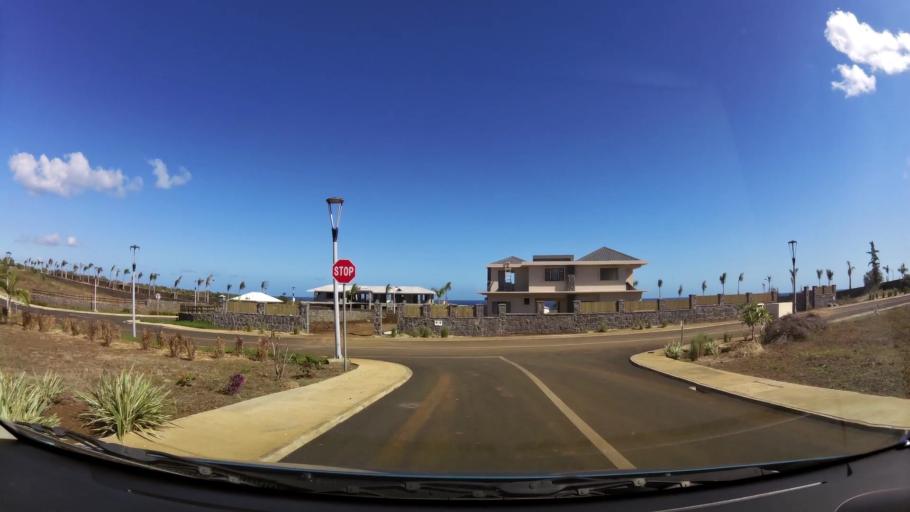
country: MU
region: Black River
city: Flic en Flac
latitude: -20.2688
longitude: 57.3828
